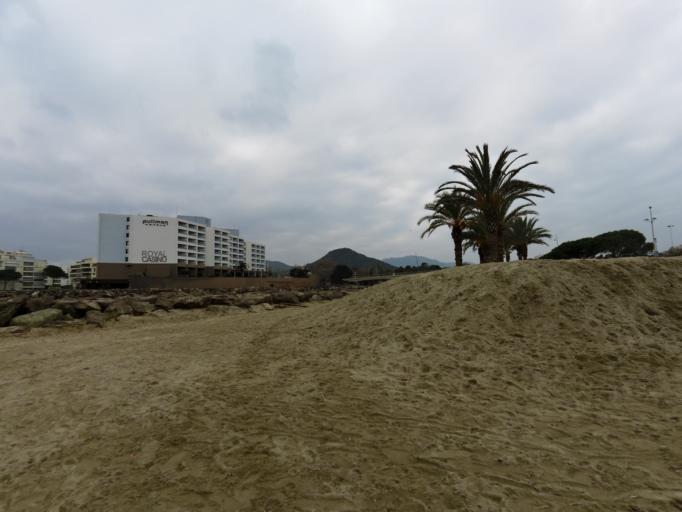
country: FR
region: Provence-Alpes-Cote d'Azur
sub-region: Departement des Alpes-Maritimes
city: Mandelieu-la-Napoule
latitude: 43.5314
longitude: 6.9495
